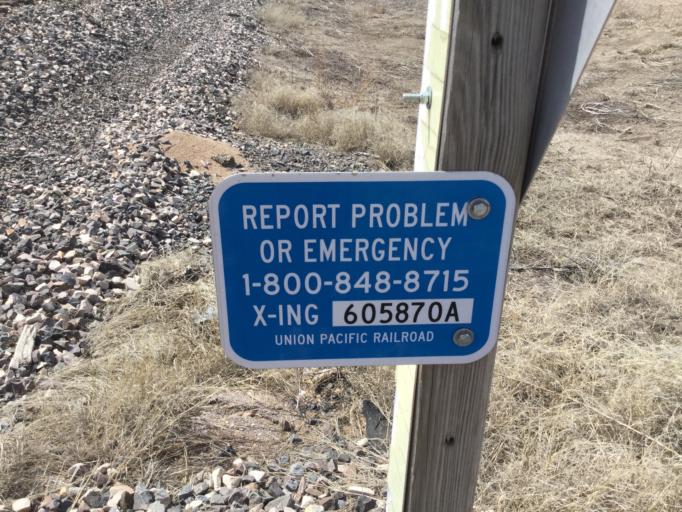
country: US
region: Kansas
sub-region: Kiowa County
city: Greensburg
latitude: 37.6187
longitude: -99.0518
